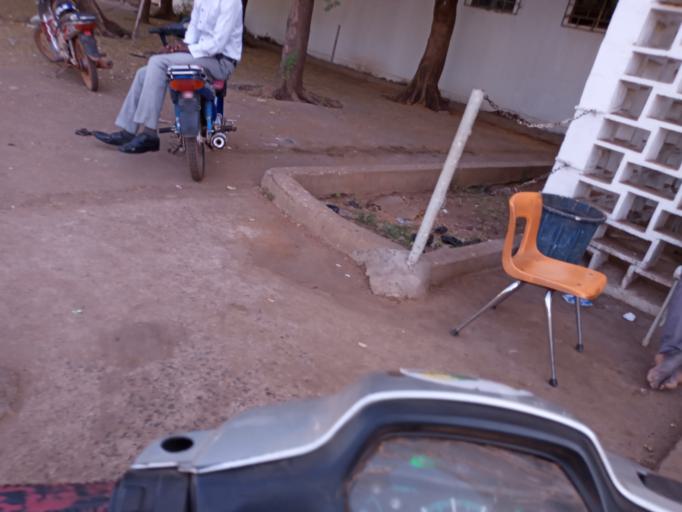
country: ML
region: Bamako
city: Bamako
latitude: 12.6317
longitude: -8.0013
